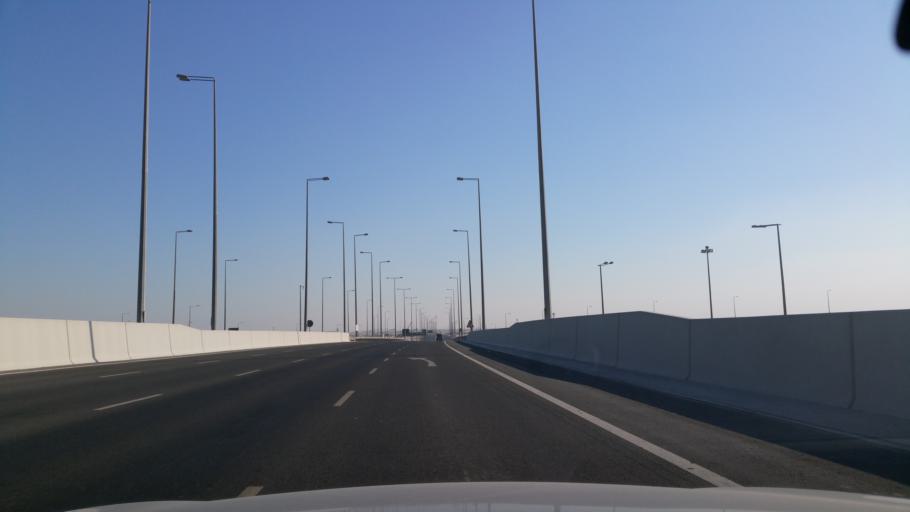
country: QA
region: Al Wakrah
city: Al Wukayr
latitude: 25.1661
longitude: 51.4719
